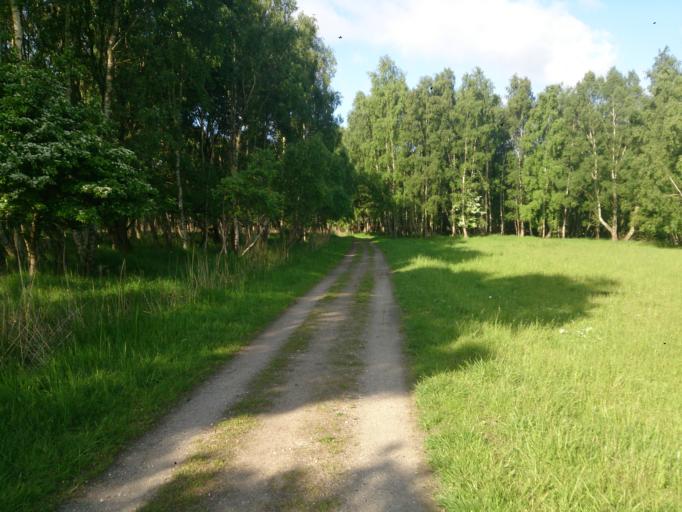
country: DK
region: Capital Region
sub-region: Tarnby Kommune
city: Tarnby
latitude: 55.5966
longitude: 12.5593
